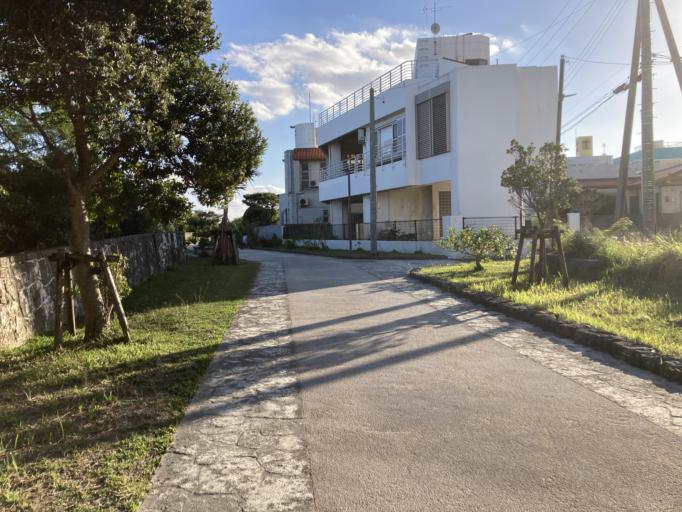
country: JP
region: Okinawa
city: Ginowan
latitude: 26.2515
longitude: 127.7761
